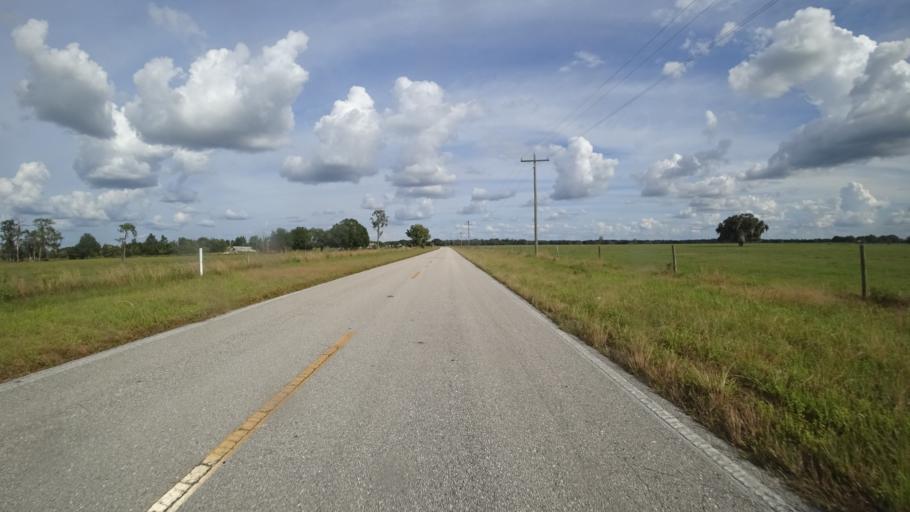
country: US
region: Florida
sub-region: Sarasota County
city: Lake Sarasota
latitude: 27.3391
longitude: -82.1843
